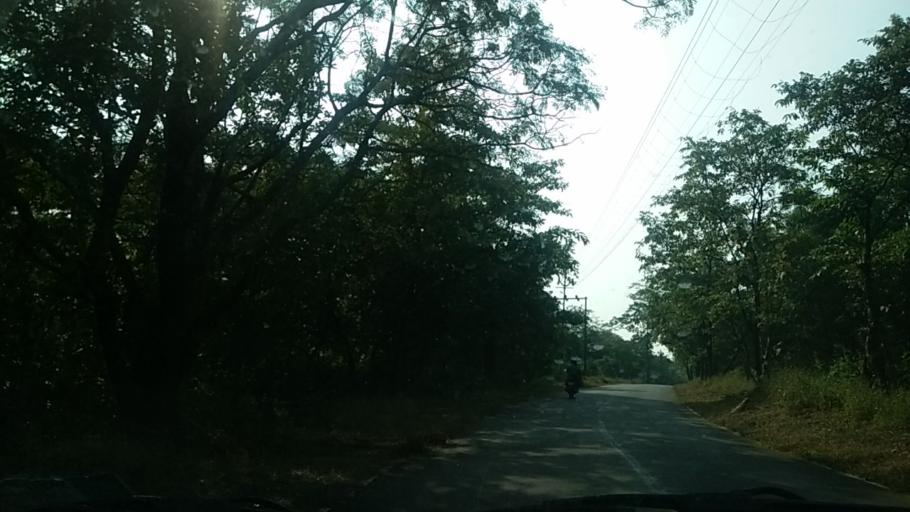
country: IN
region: Goa
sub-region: South Goa
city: Sanguem
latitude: 15.1953
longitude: 74.2278
